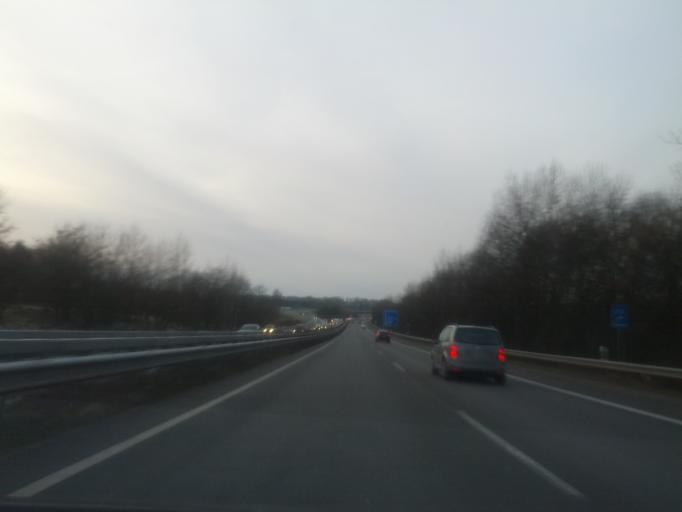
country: DE
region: Lower Saxony
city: Buchholz in der Nordheide
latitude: 53.3720
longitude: 9.8978
